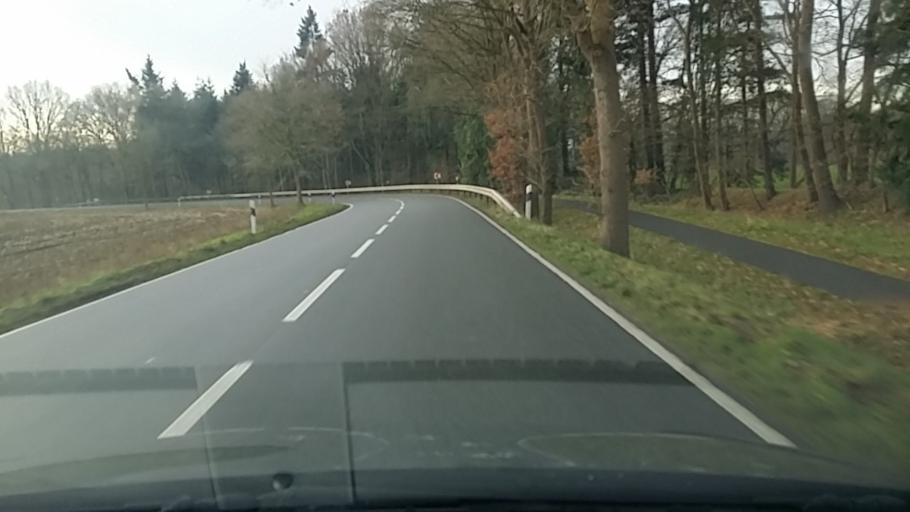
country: DE
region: Lower Saxony
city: Loningen
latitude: 52.7201
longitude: 7.7893
